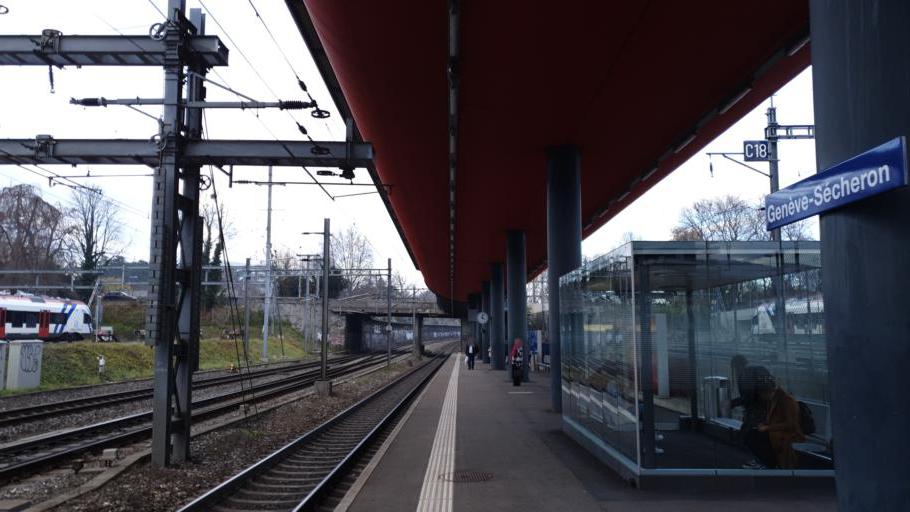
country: CH
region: Geneva
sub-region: Geneva
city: Geneve
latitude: 46.2224
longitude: 6.1447
